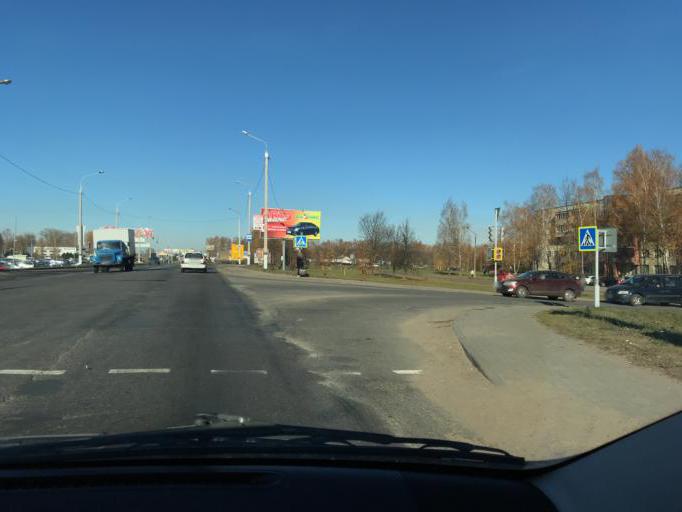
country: BY
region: Vitebsk
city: Polatsk
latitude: 55.4712
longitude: 28.7526
